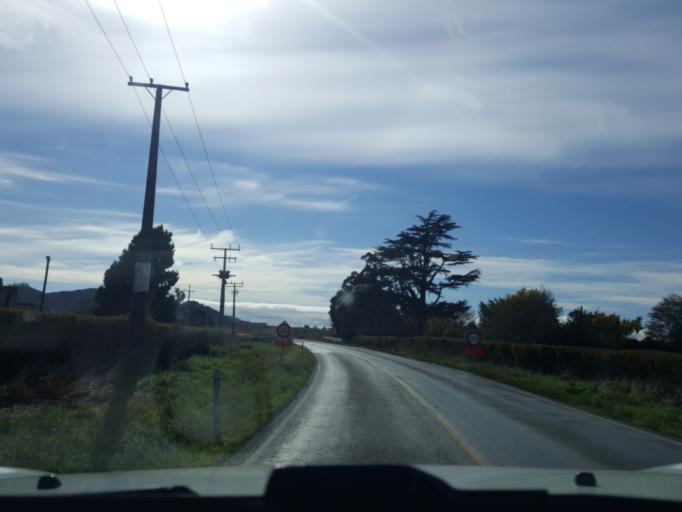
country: NZ
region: Waikato
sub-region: Waikato District
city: Ngaruawahia
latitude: -37.6012
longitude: 175.2020
